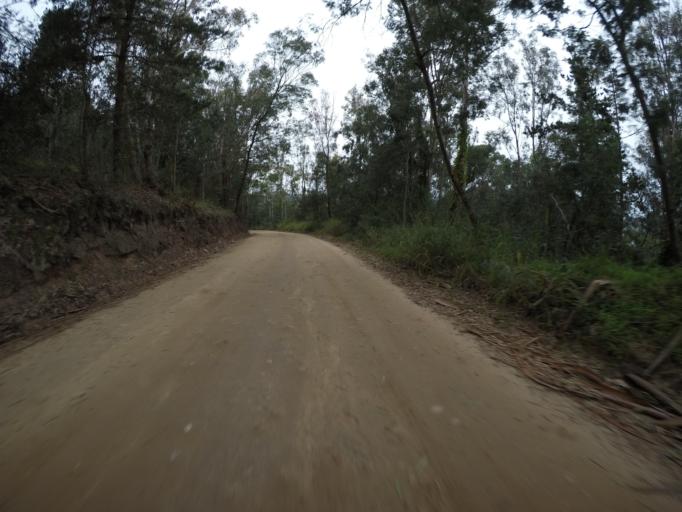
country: ZA
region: Western Cape
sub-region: Eden District Municipality
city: Knysna
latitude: -34.0112
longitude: 22.8064
